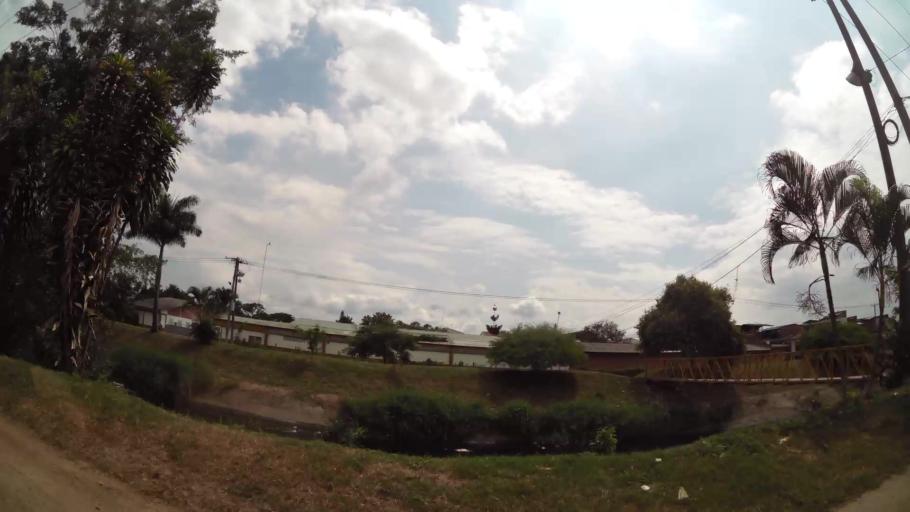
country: CO
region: Valle del Cauca
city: Cali
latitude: 3.4891
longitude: -76.4862
